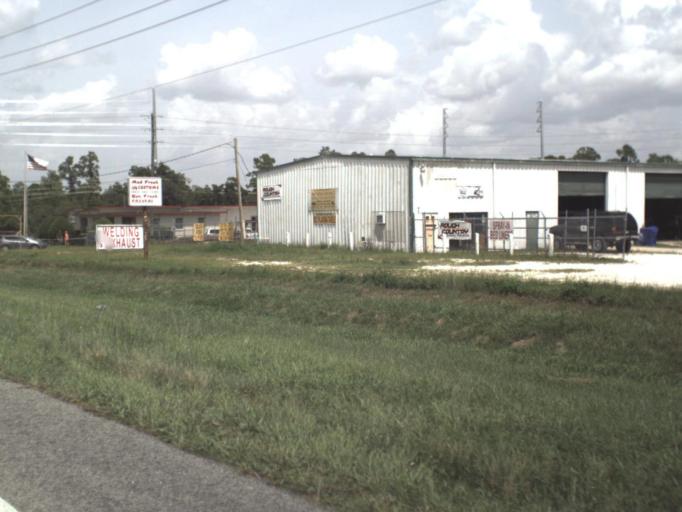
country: US
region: Florida
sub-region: Highlands County
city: Sebring
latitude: 27.5284
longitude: -81.4999
